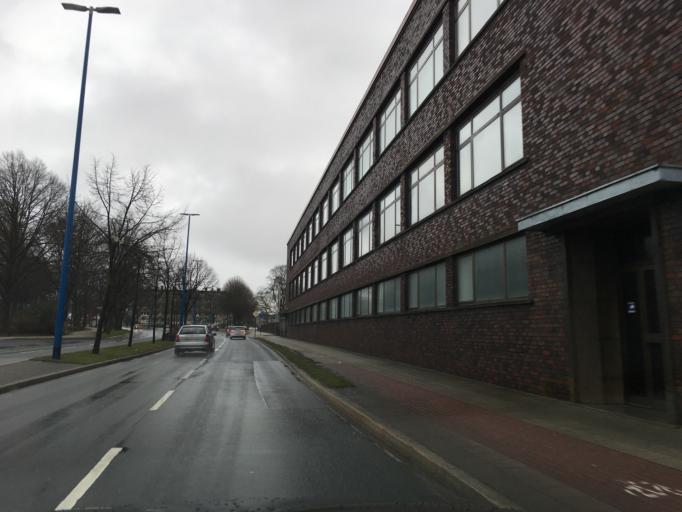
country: DE
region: North Rhine-Westphalia
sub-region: Regierungsbezirk Dusseldorf
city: Velbert
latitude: 51.3314
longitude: 7.0421
